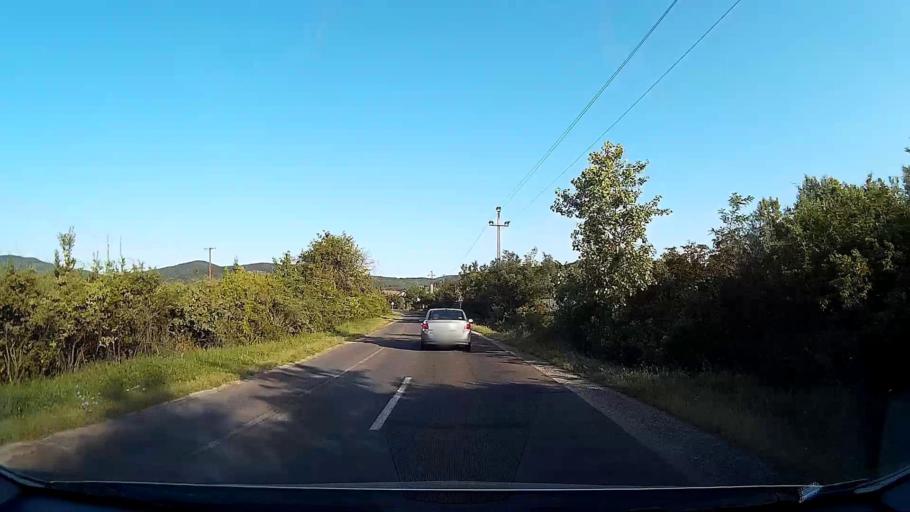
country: HU
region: Pest
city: Szentendre
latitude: 47.6955
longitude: 19.0434
